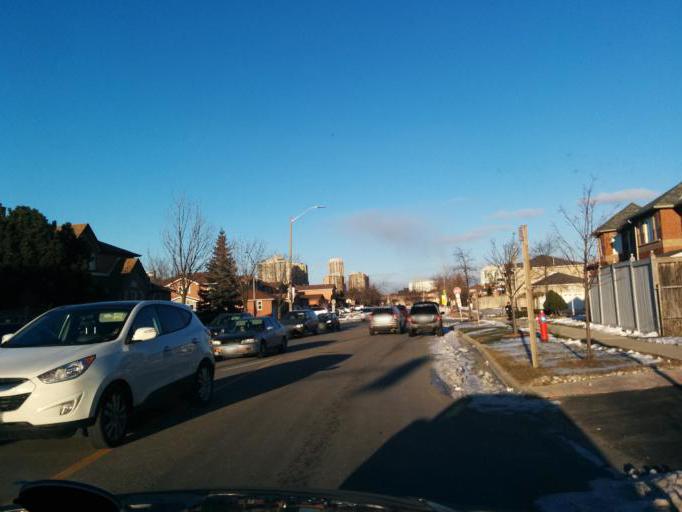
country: CA
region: Ontario
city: Mississauga
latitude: 43.5947
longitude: -79.6584
